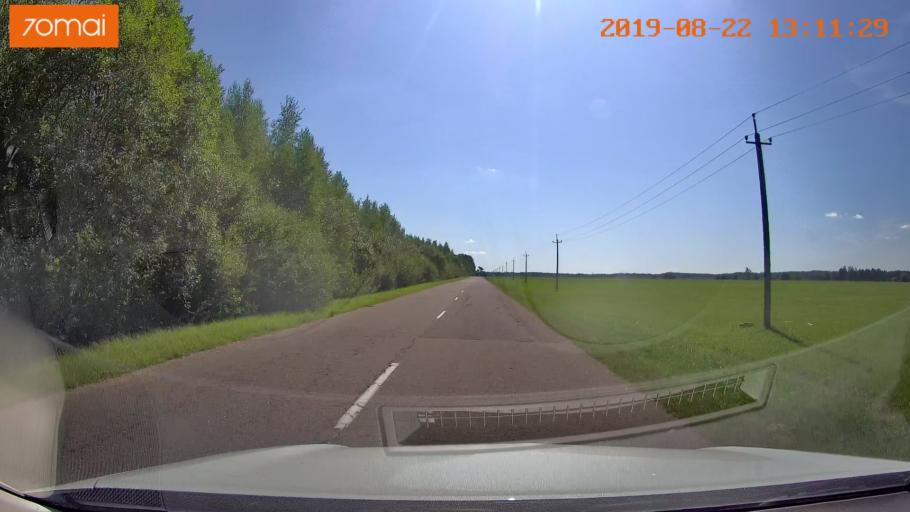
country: BY
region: Minsk
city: Prawdzinski
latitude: 53.2801
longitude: 27.8531
